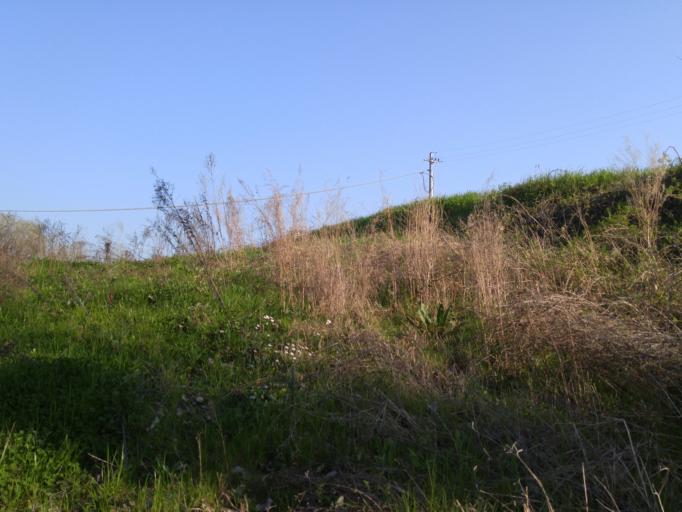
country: IT
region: The Marches
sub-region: Provincia di Pesaro e Urbino
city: Lucrezia
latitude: 43.7736
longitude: 12.9304
